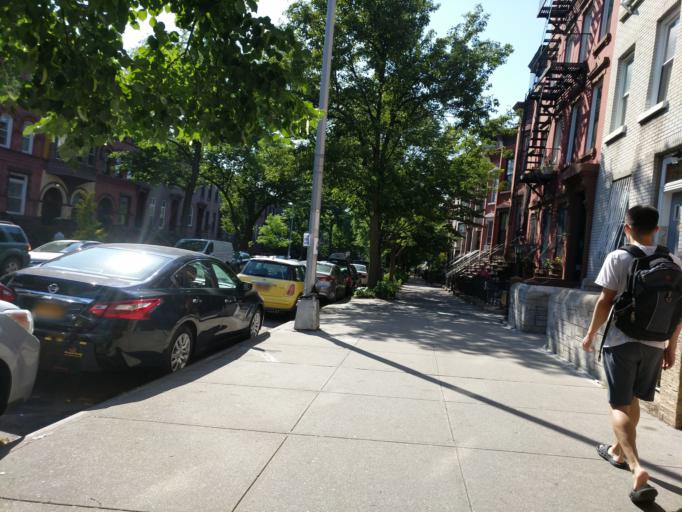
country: US
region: New York
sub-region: Kings County
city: Brooklyn
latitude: 40.6756
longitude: -73.9784
